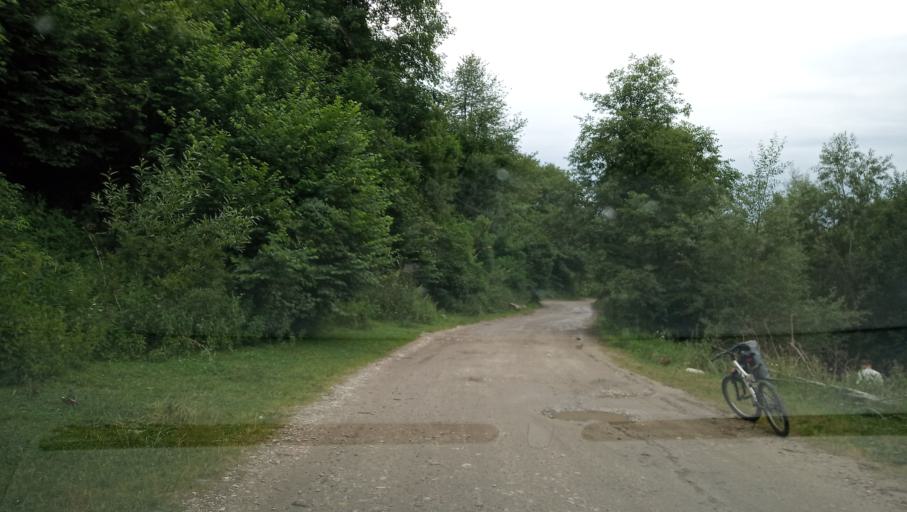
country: RO
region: Hunedoara
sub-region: Oras Petrila
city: Petrila
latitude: 45.4686
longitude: 23.4197
